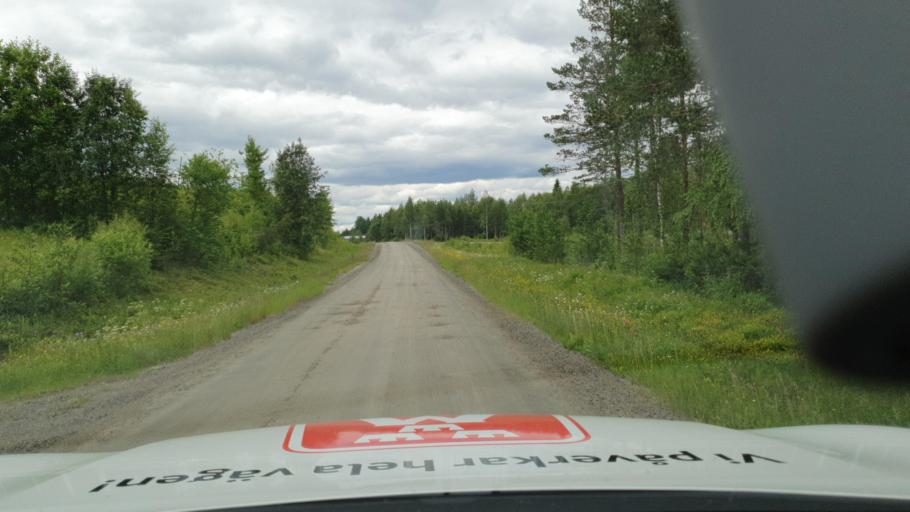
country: SE
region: Vaesterbotten
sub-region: Bjurholms Kommun
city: Bjurholm
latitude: 63.7285
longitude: 19.3067
